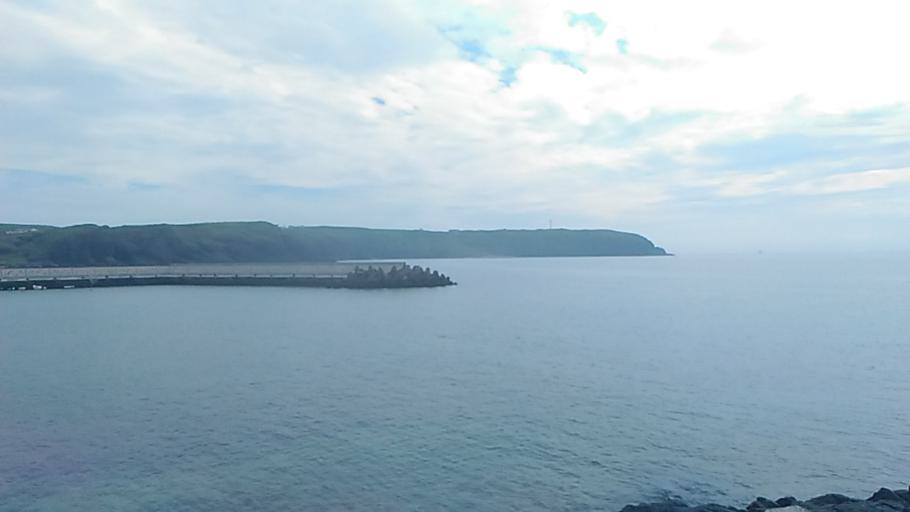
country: TW
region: Taiwan
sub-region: Penghu
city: Ma-kung
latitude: 23.1925
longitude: 119.4294
